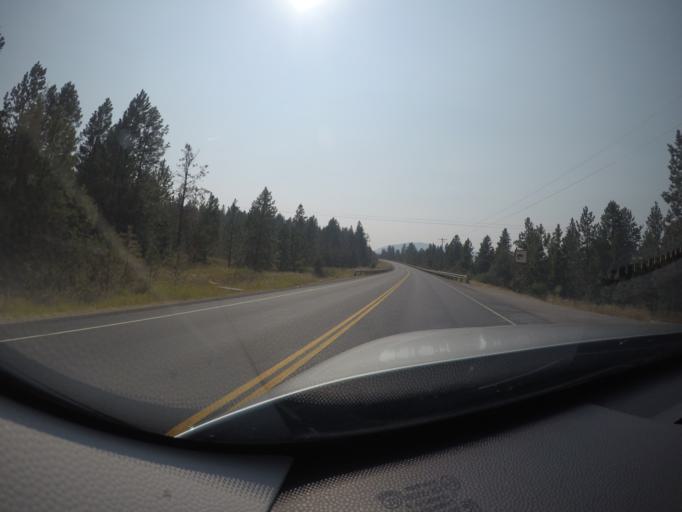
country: US
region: Montana
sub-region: Lake County
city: Polson
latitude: 47.8112
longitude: -114.2632
